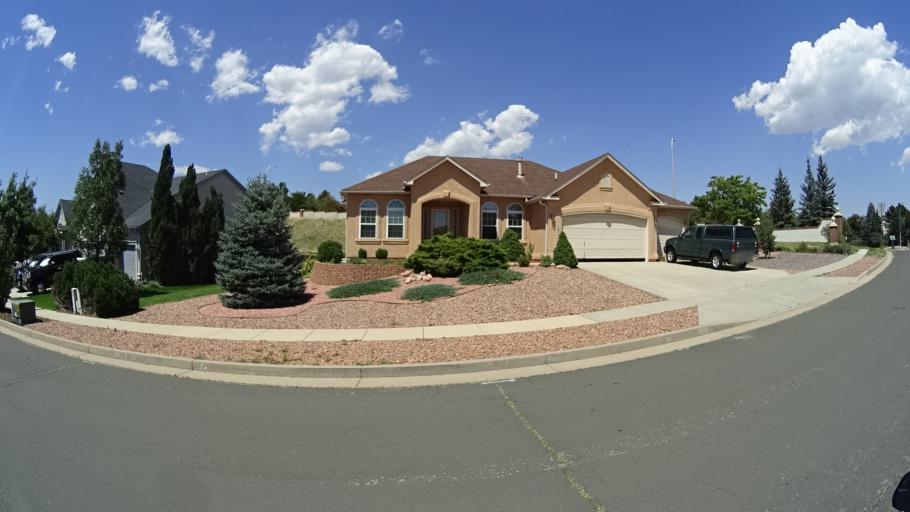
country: US
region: Colorado
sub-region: El Paso County
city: Black Forest
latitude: 38.9562
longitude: -104.7572
